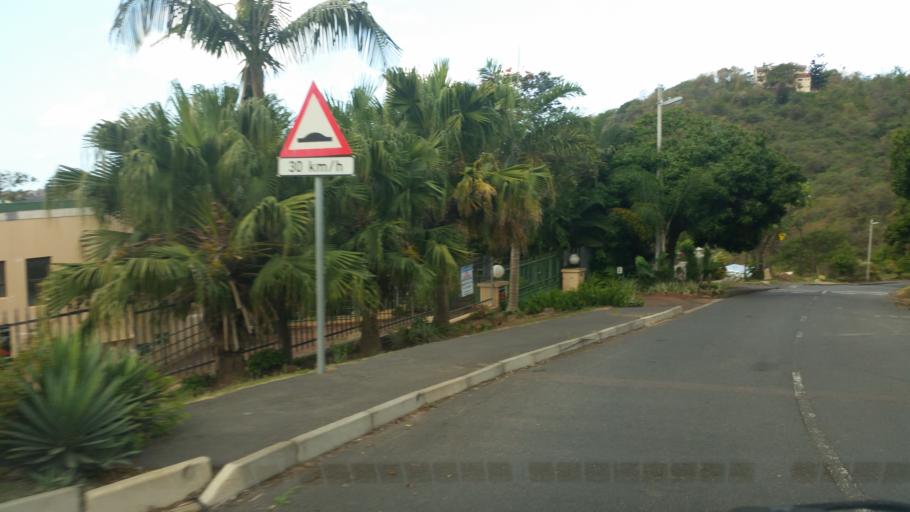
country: ZA
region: KwaZulu-Natal
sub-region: eThekwini Metropolitan Municipality
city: Berea
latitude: -29.8251
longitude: 30.9482
